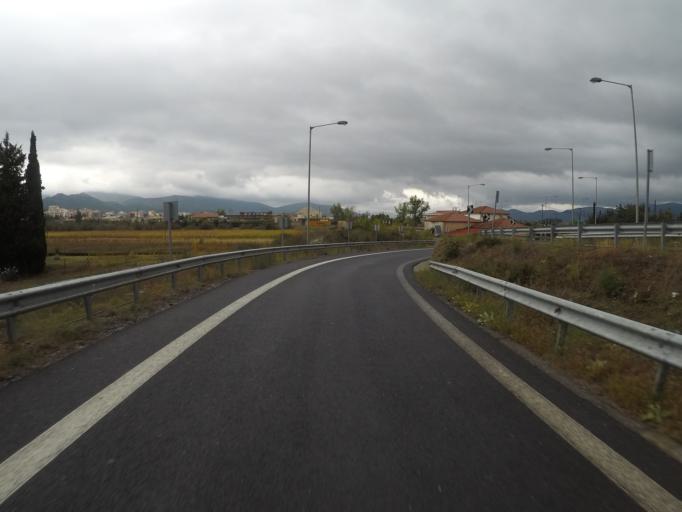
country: GR
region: Peloponnese
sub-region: Nomos Arkadias
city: Tripoli
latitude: 37.4946
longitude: 22.3780
